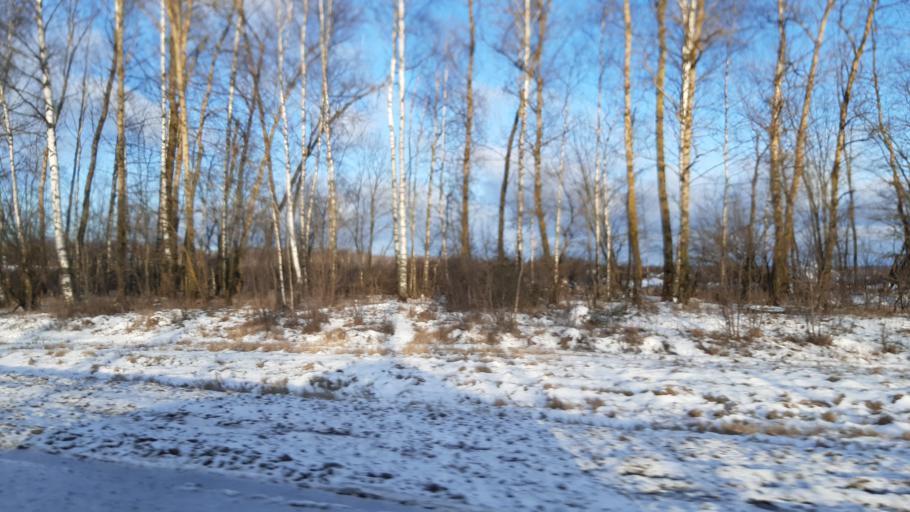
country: RU
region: Vladimir
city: Arsaki
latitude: 56.2879
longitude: 38.3889
